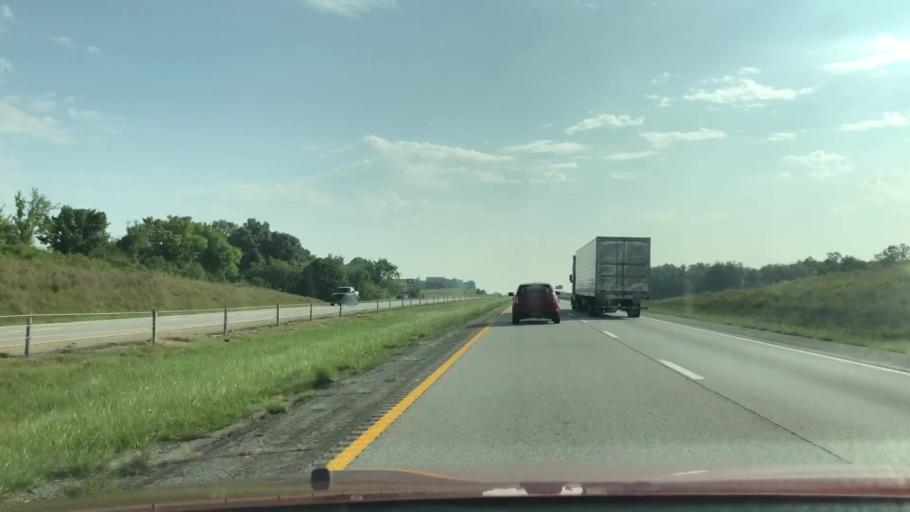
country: US
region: Missouri
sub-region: Laclede County
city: Lebanon
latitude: 37.5847
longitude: -92.7362
